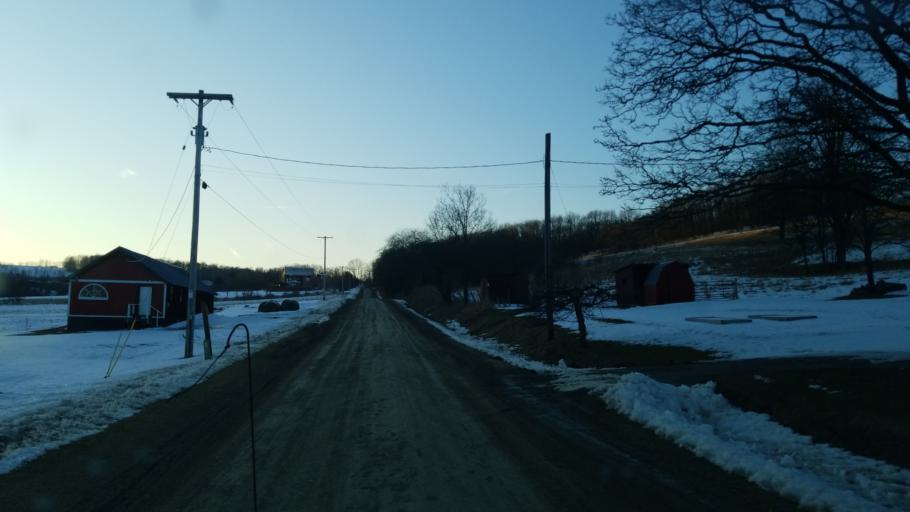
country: US
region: Pennsylvania
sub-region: Tioga County
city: Westfield
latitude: 42.0403
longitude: -77.5939
